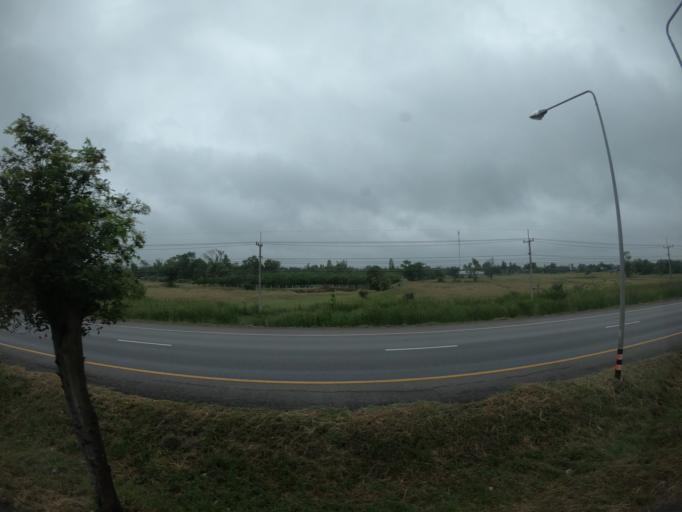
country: TH
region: Nakhon Ratchasima
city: Phimai
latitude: 15.3171
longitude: 102.4315
